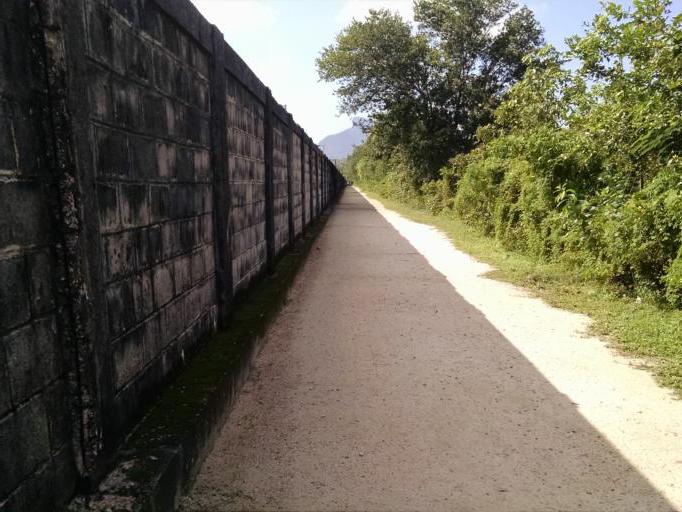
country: BR
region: Rio de Janeiro
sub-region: Rio De Janeiro
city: Rio de Janeiro
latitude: -22.9935
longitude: -43.3724
